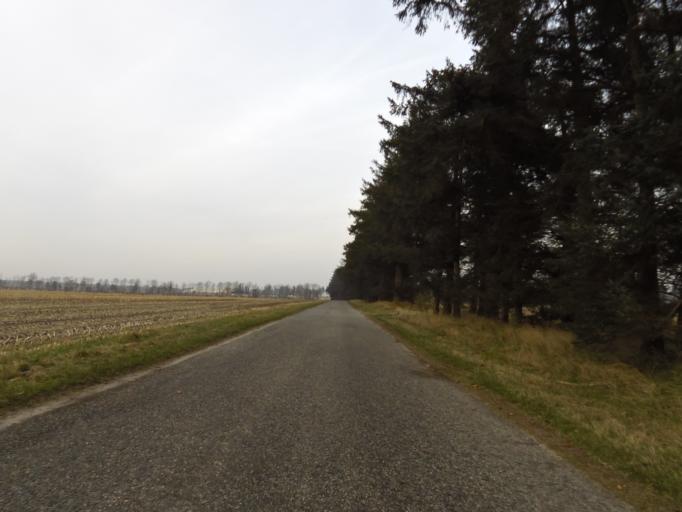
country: DK
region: South Denmark
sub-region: Esbjerg Kommune
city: Ribe
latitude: 55.3397
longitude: 8.8938
